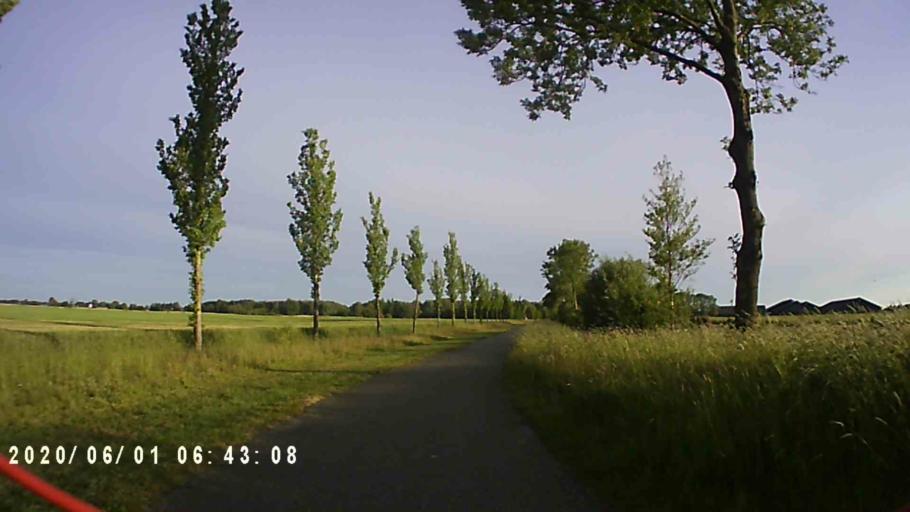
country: NL
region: Friesland
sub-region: Gemeente Kollumerland en Nieuwkruisland
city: Kollum
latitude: 53.2969
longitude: 6.1529
